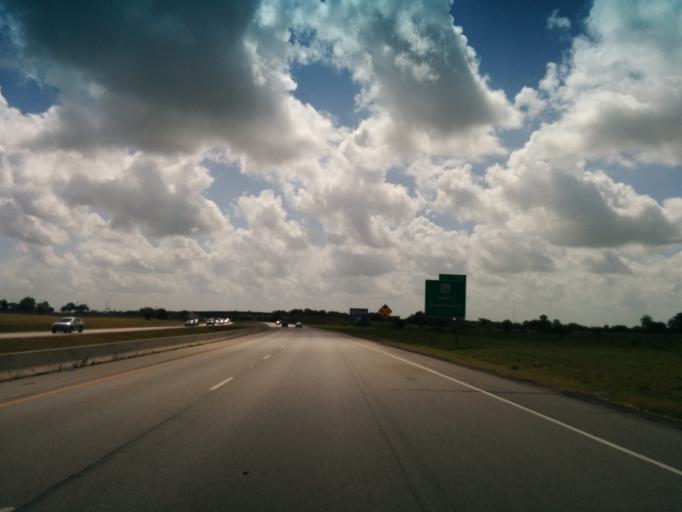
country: US
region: Texas
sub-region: Austin County
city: Sealy
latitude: 29.7600
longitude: -96.1755
